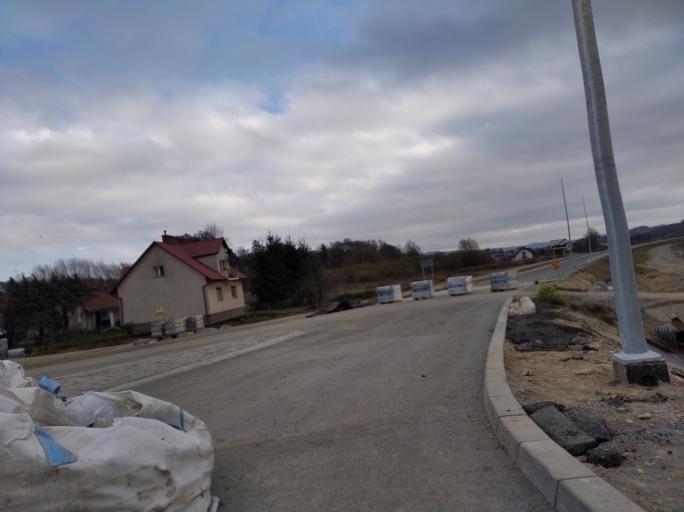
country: PL
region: Subcarpathian Voivodeship
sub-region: Powiat strzyzowski
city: Strzyzow
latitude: 49.8741
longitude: 21.7632
